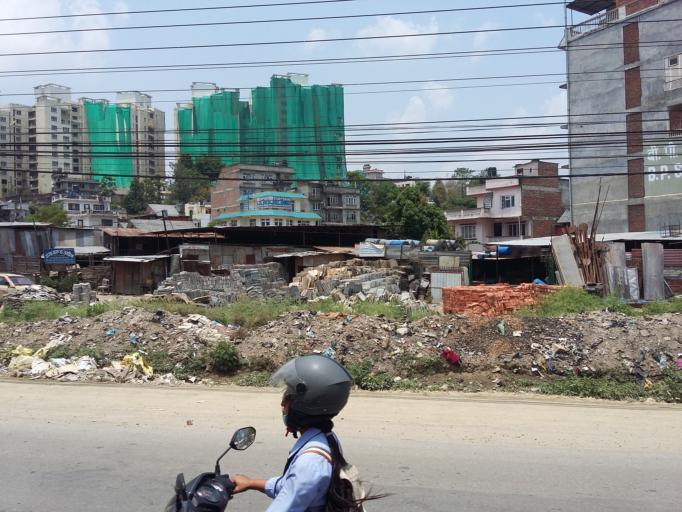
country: NP
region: Central Region
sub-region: Bagmati Zone
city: Kathmandu
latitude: 27.7391
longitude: 85.3268
